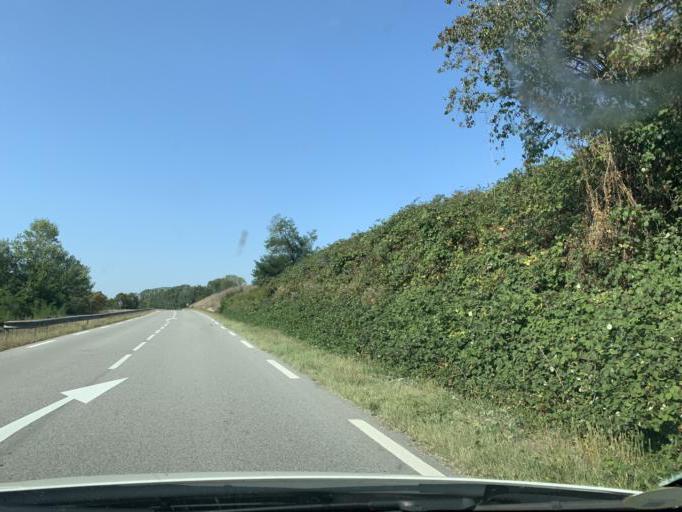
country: FR
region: Rhone-Alpes
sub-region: Departement de la Savoie
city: Saint-Genix-sur-Guiers
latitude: 45.6399
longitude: 5.6654
